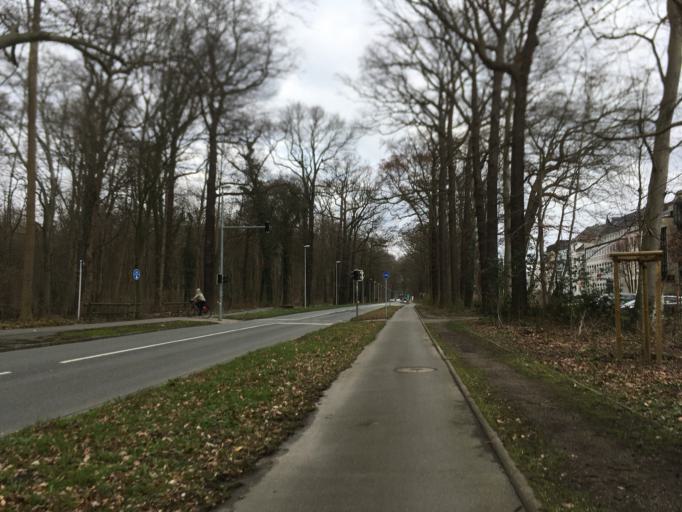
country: DE
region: Lower Saxony
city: Hannover
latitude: 52.3790
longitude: 9.7592
